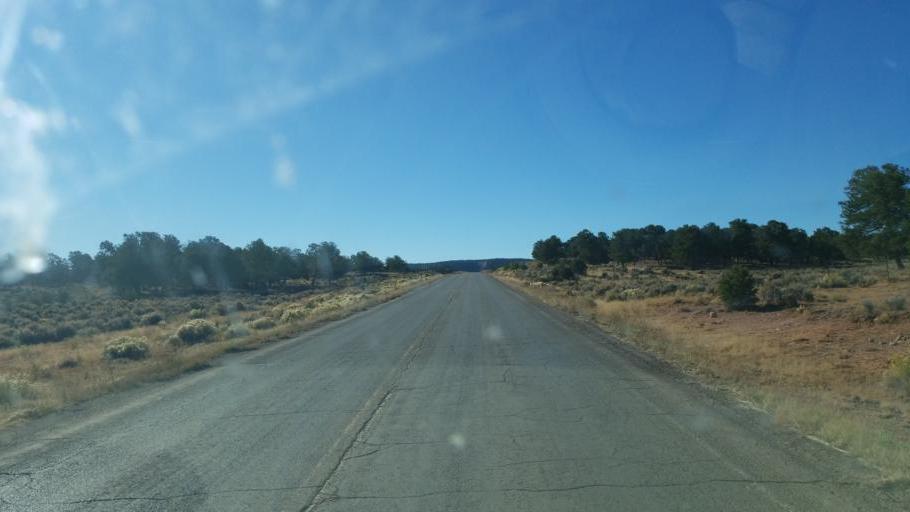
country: US
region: New Mexico
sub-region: McKinley County
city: Navajo
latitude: 35.9975
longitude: -109.0173
